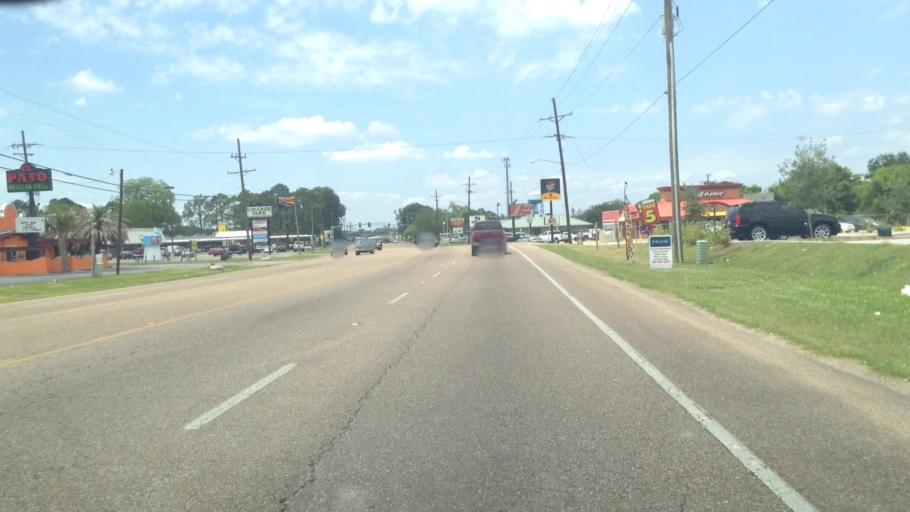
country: US
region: Louisiana
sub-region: Iberia Parish
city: New Iberia
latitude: 29.9878
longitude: -91.8249
